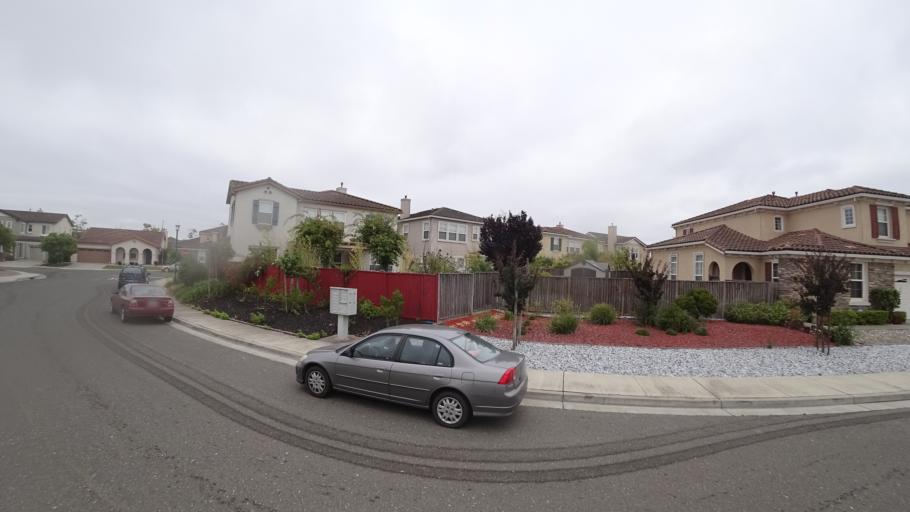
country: US
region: California
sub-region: Alameda County
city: Hayward
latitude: 37.6121
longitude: -122.0946
